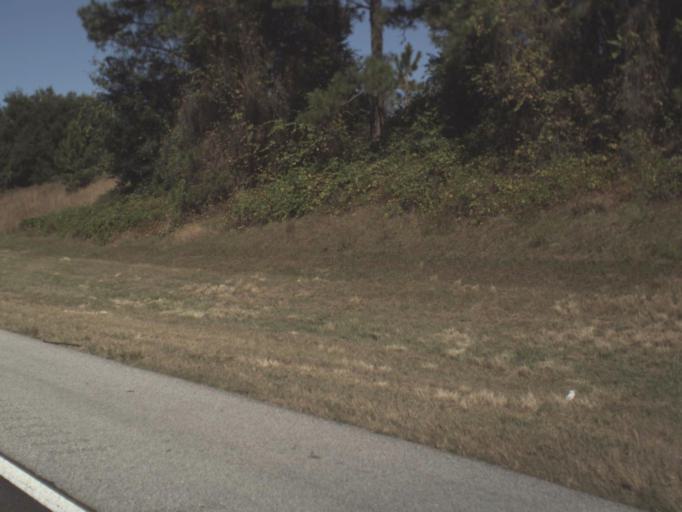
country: US
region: Florida
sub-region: Lake County
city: Minneola
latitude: 28.6362
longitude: -81.7790
